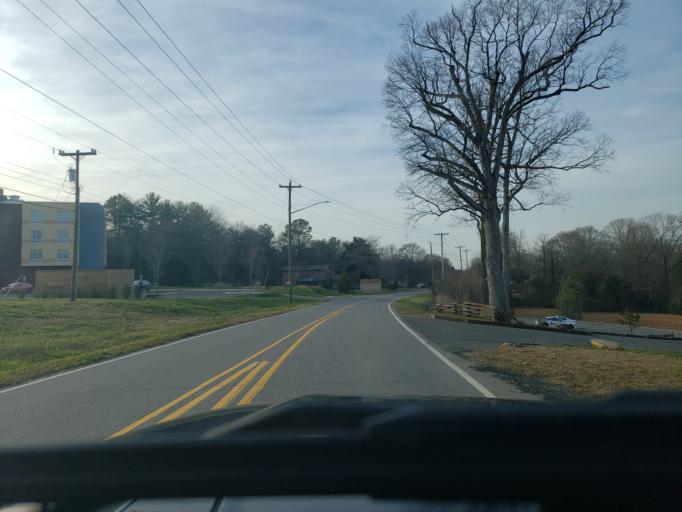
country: US
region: North Carolina
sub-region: Cleveland County
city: Shelby
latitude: 35.2744
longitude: -81.5022
